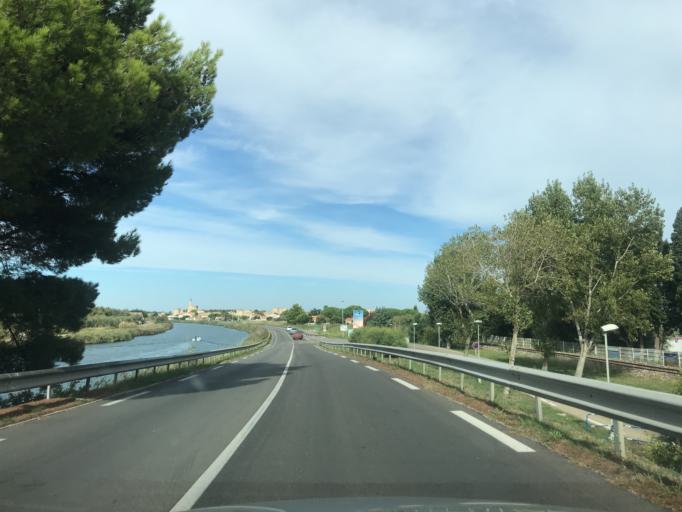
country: FR
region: Languedoc-Roussillon
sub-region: Departement du Gard
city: Aigues-Mortes
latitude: 43.5577
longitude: 4.1823
